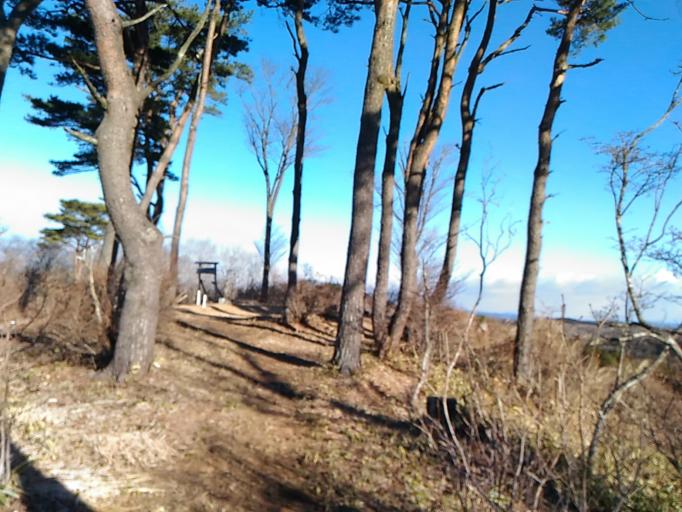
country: JP
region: Fukushima
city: Ishikawa
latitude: 36.9575
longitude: 140.5836
